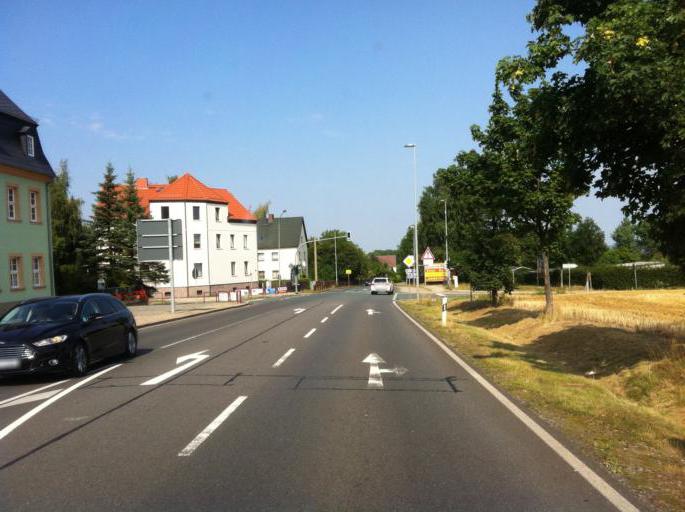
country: DE
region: Saxony
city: Lichtentanne
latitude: 50.6963
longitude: 12.4330
